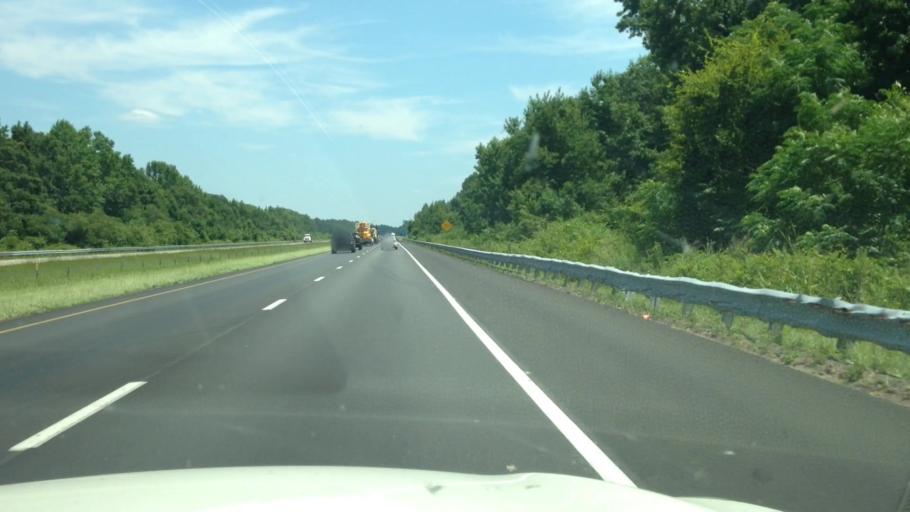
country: US
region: South Carolina
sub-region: Florence County
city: Timmonsville
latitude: 34.2017
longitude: -80.0651
